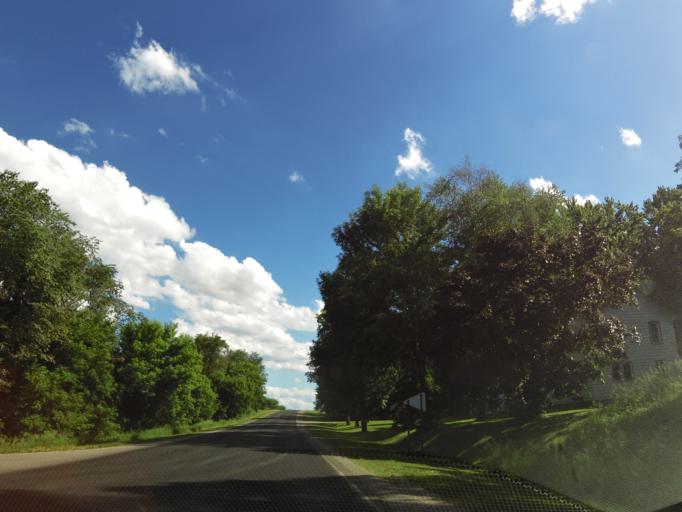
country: US
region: Minnesota
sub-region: Meeker County
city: Dassel
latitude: 45.1281
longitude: -94.2968
